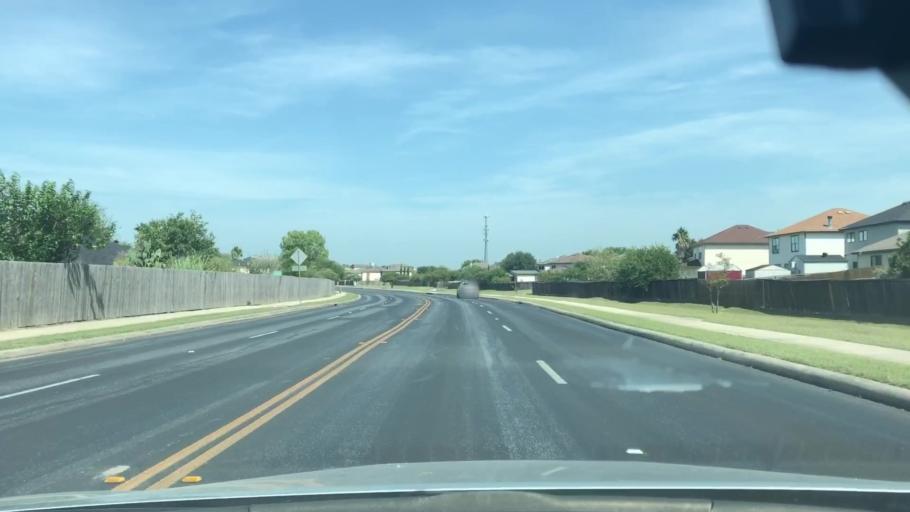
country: US
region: Texas
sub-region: Bexar County
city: Converse
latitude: 29.4937
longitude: -98.3155
